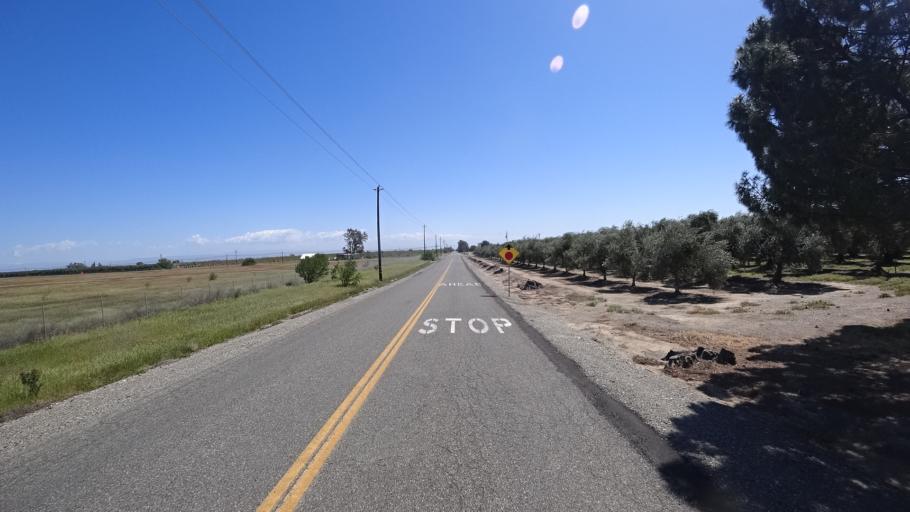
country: US
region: California
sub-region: Glenn County
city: Orland
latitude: 39.7107
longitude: -122.1434
